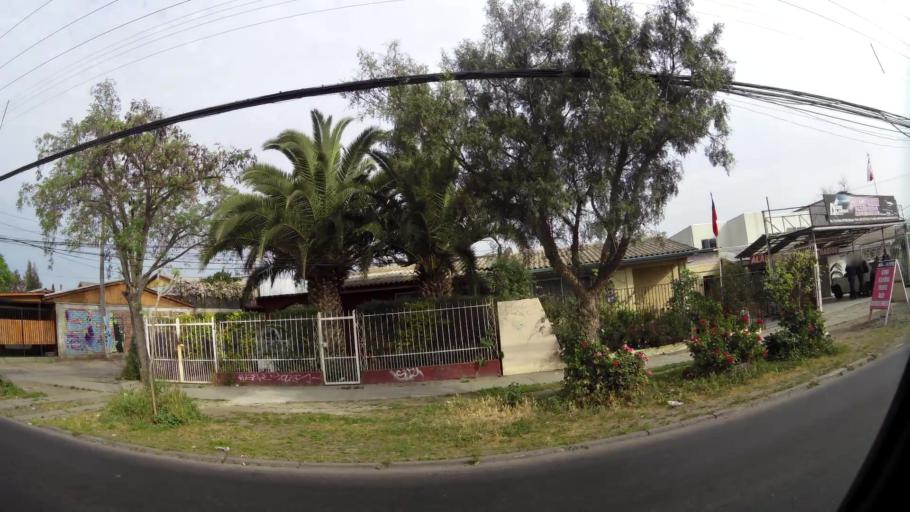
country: CL
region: Santiago Metropolitan
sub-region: Provincia de Santiago
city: Lo Prado
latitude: -33.5174
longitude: -70.7630
